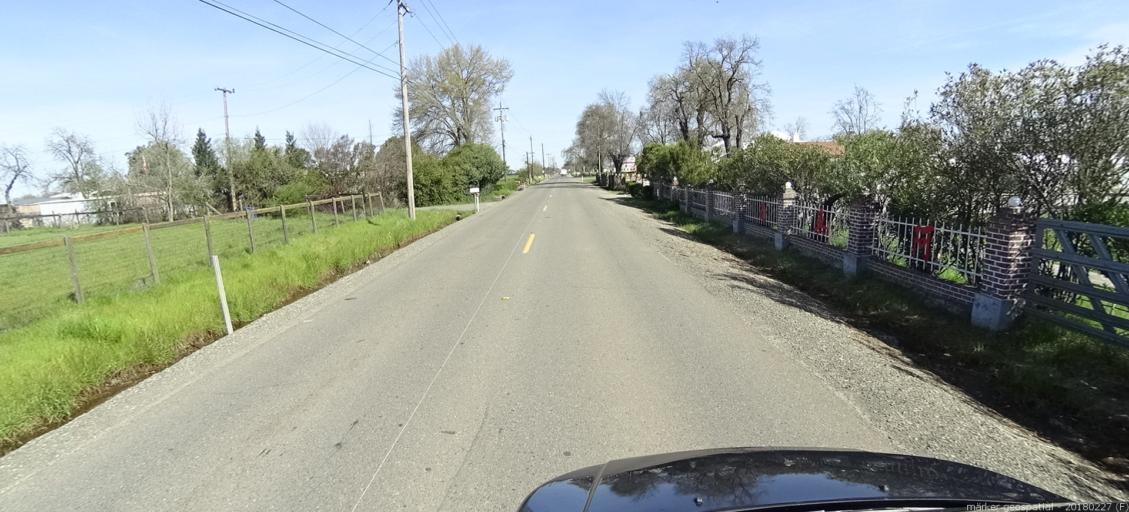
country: US
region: California
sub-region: Sacramento County
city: Vineyard
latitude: 38.5039
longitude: -121.3627
